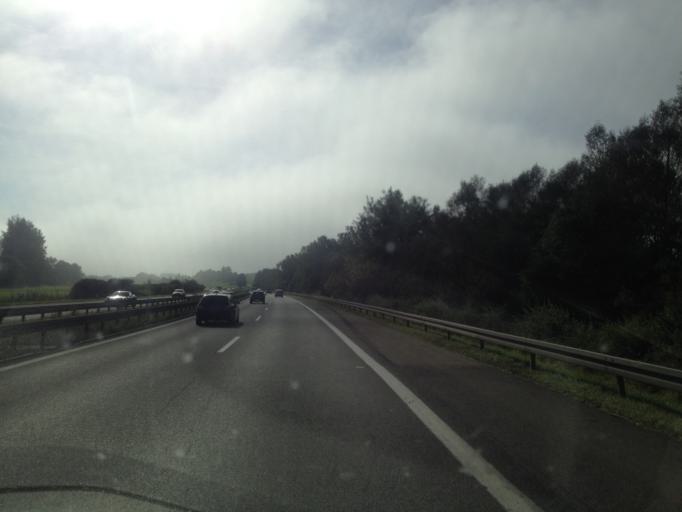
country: DE
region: Baden-Wuerttemberg
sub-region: Freiburg Region
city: Geisingen
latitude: 47.9412
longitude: 8.6211
